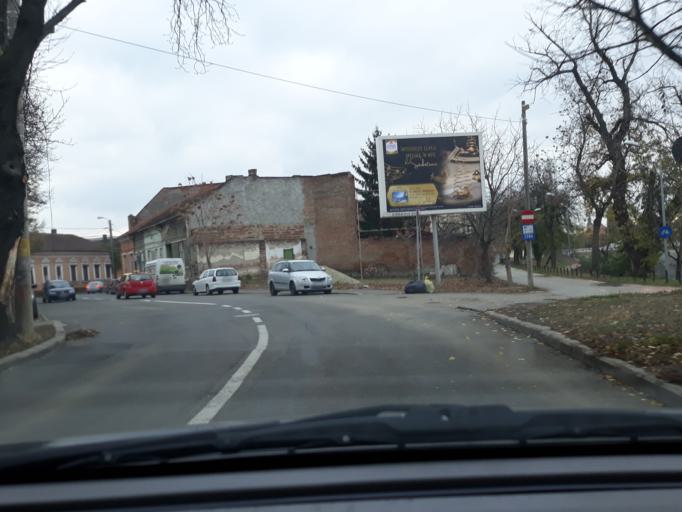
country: RO
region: Bihor
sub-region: Comuna Biharea
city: Oradea
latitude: 47.0634
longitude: 21.9254
